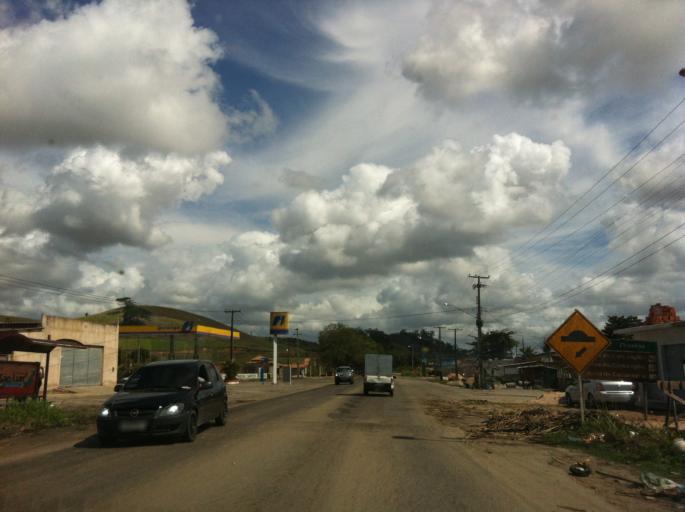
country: BR
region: Alagoas
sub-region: Sao Luis Do Quitunde
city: Sao Luis do Quitunde
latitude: -9.2968
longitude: -35.5650
